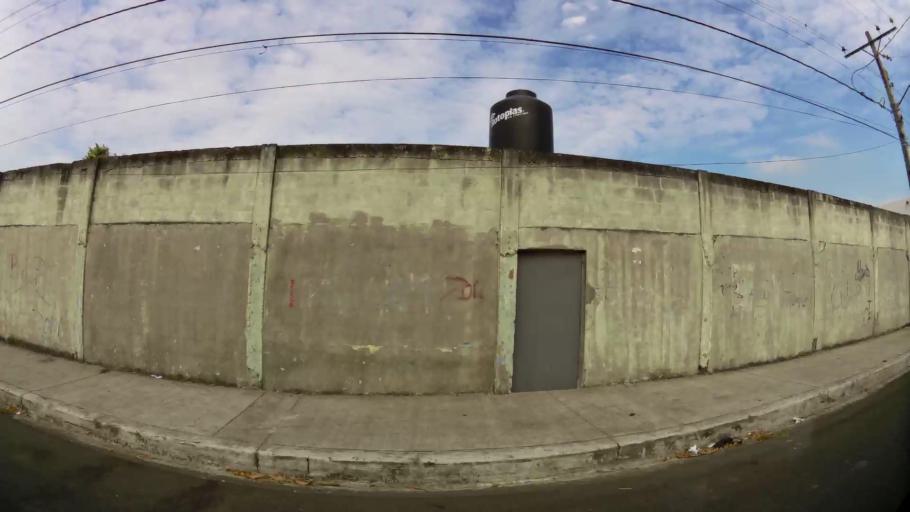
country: EC
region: Guayas
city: Guayaquil
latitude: -2.2457
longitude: -79.8837
